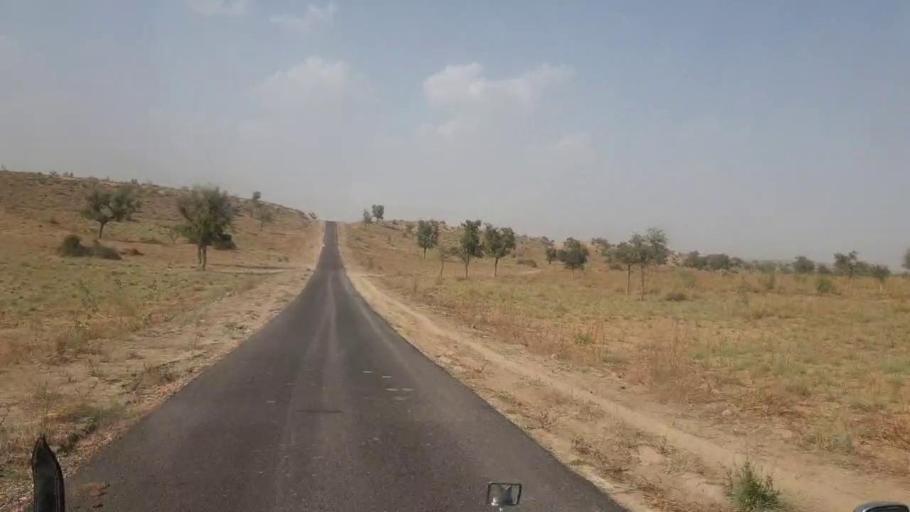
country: PK
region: Sindh
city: Islamkot
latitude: 25.1911
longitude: 70.2854
